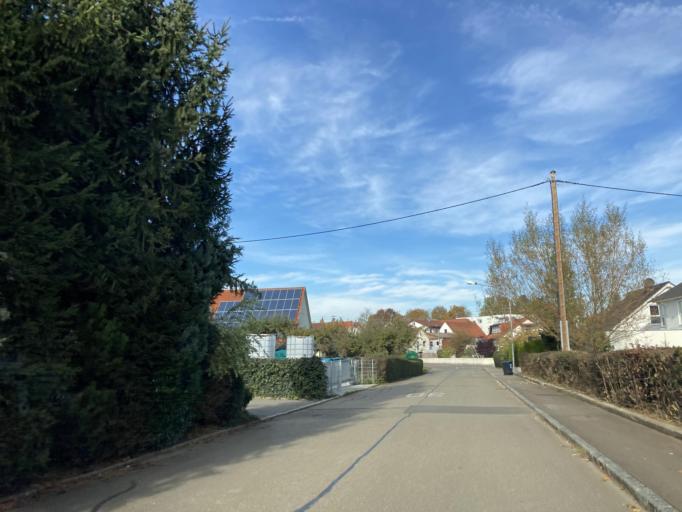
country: DE
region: Baden-Wuerttemberg
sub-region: Tuebingen Region
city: Bodelshausen
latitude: 48.3922
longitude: 8.9775
